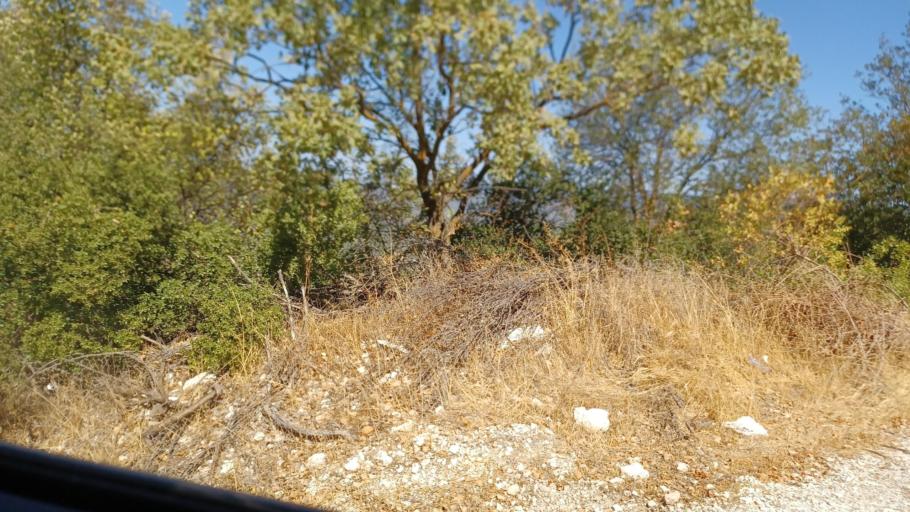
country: CY
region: Pafos
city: Mesogi
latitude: 34.9083
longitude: 32.6257
